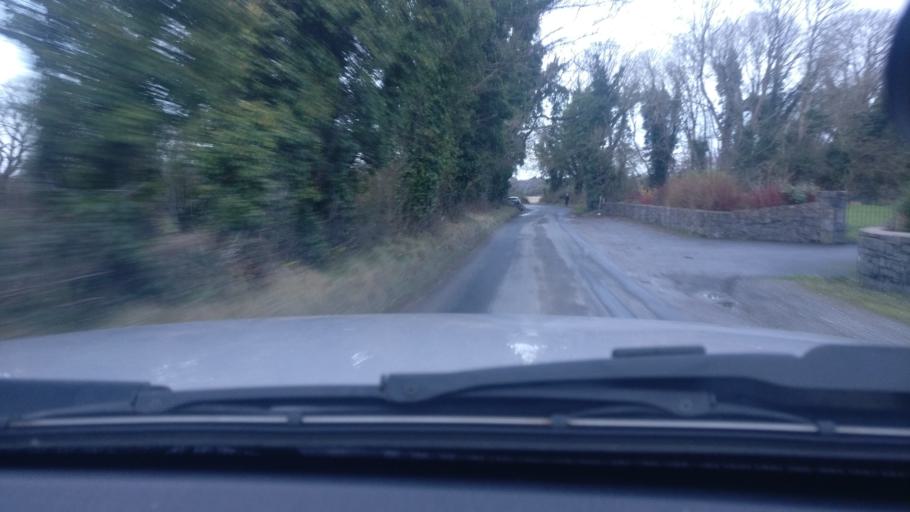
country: IE
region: Connaught
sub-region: County Galway
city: Loughrea
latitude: 53.1928
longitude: -8.5096
